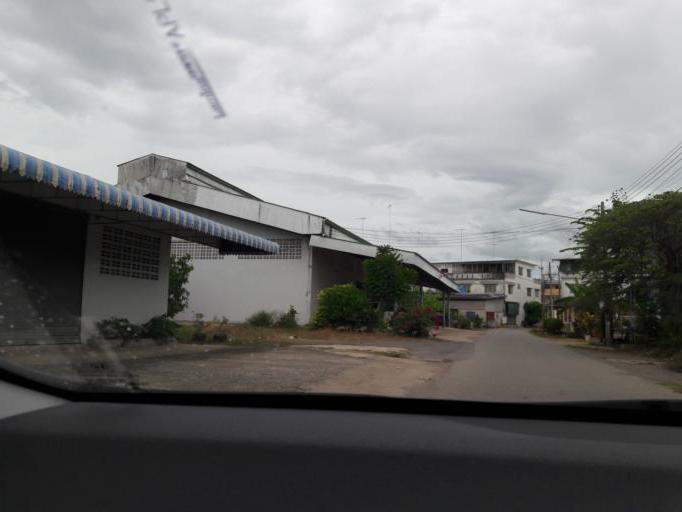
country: TH
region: Samut Sakhon
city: Ban Phaeo
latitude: 13.5533
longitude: 100.0378
